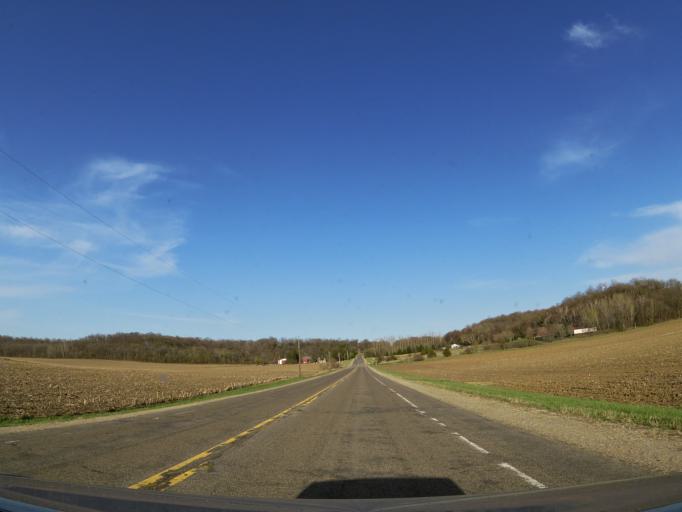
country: US
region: Minnesota
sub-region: Washington County
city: Lake Saint Croix Beach
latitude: 44.8624
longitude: -92.7090
